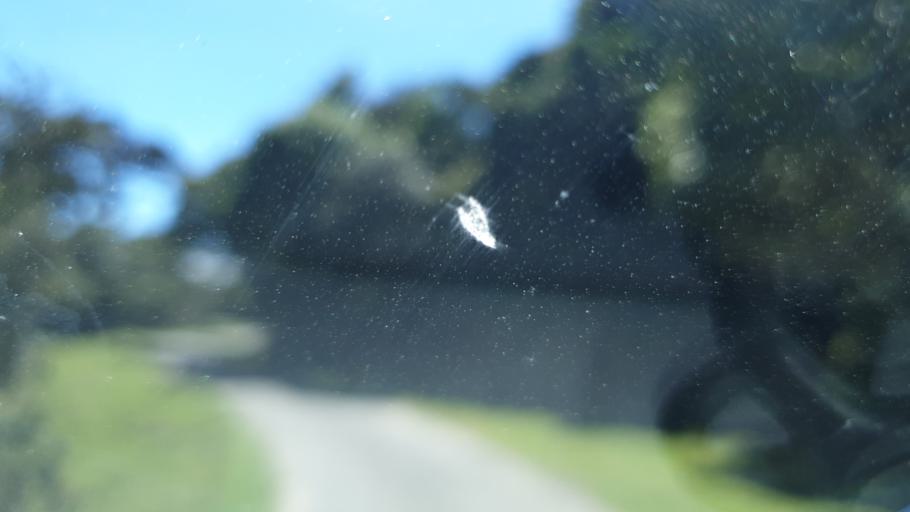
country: LK
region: Uva
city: Haputale
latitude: 6.8018
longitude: 80.8339
